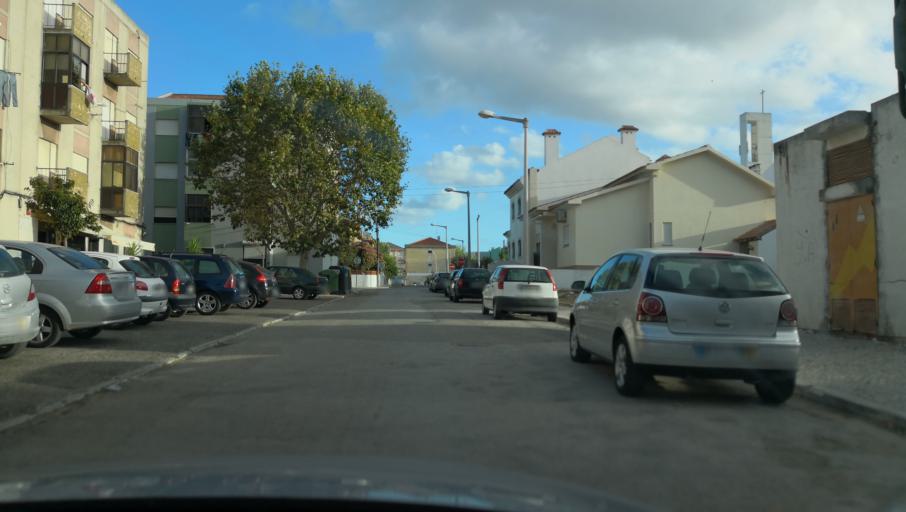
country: PT
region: Setubal
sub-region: Barreiro
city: Barreiro
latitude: 38.6694
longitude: -9.0492
